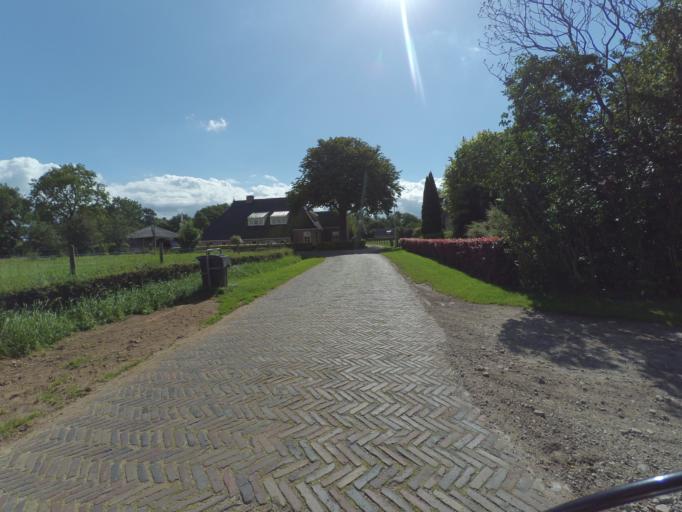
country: NL
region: Friesland
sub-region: Gemeente Achtkarspelen
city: Twijzelerheide
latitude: 53.2150
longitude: 6.0575
